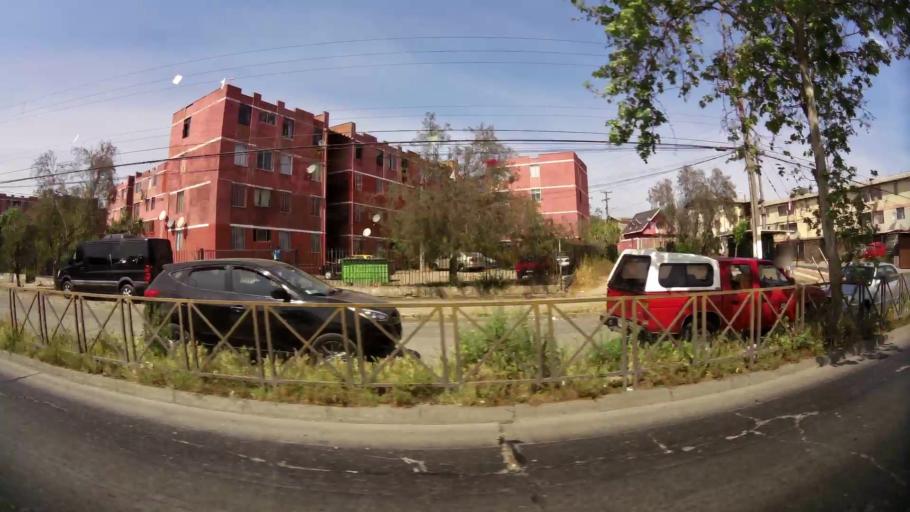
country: CL
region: Santiago Metropolitan
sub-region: Provincia de Santiago
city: Lo Prado
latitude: -33.4447
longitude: -70.7383
